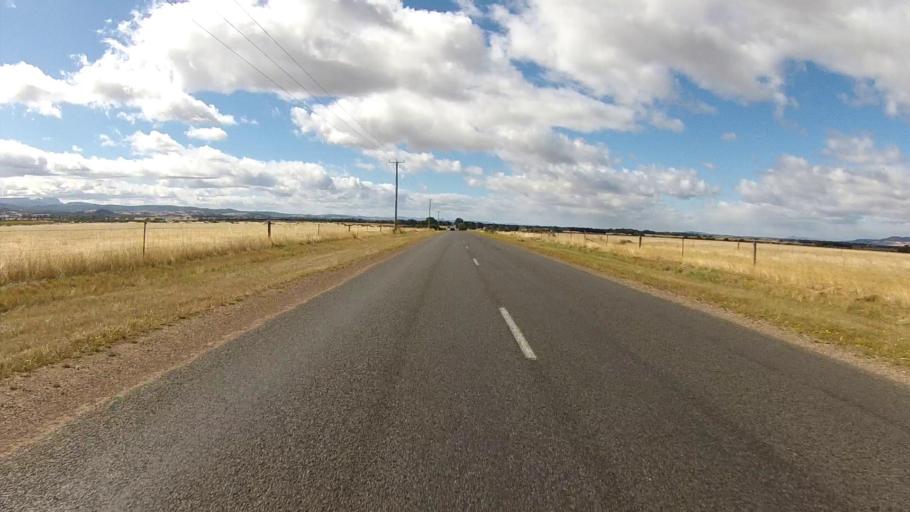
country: AU
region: Tasmania
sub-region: Northern Midlands
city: Evandale
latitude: -41.5924
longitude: 147.2666
